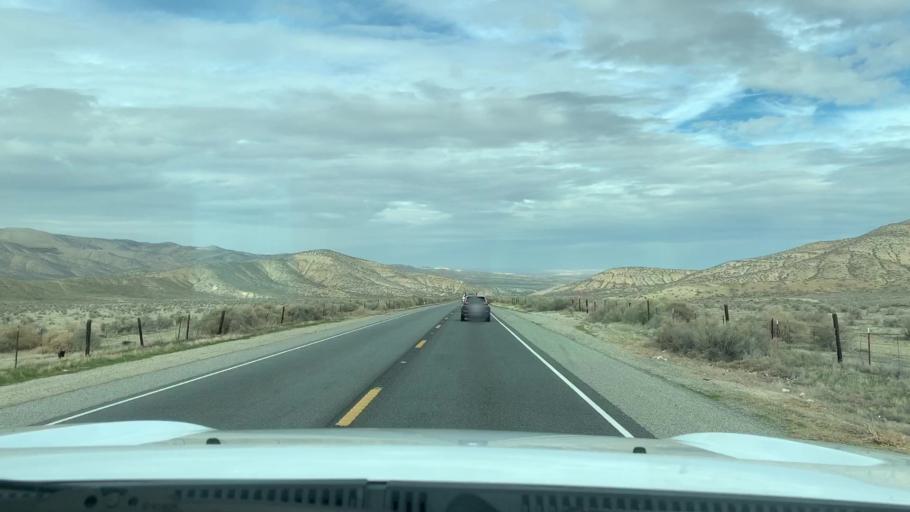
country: US
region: California
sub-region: Kern County
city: Maricopa
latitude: 35.0210
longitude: -119.4165
